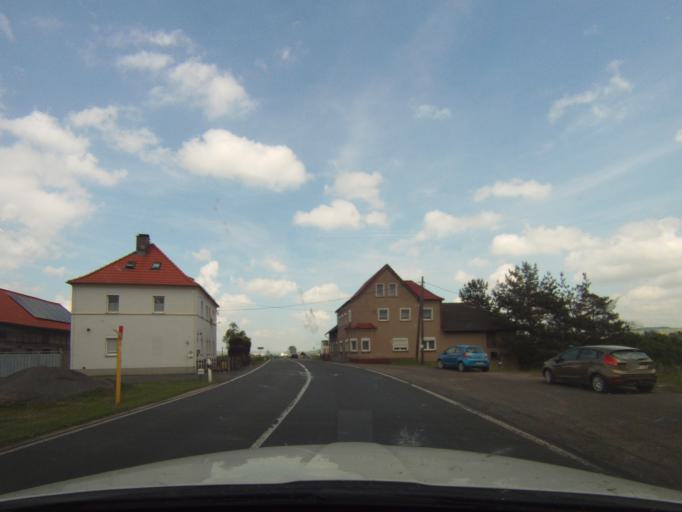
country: DE
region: Thuringia
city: Konitz
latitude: 50.6646
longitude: 11.4918
